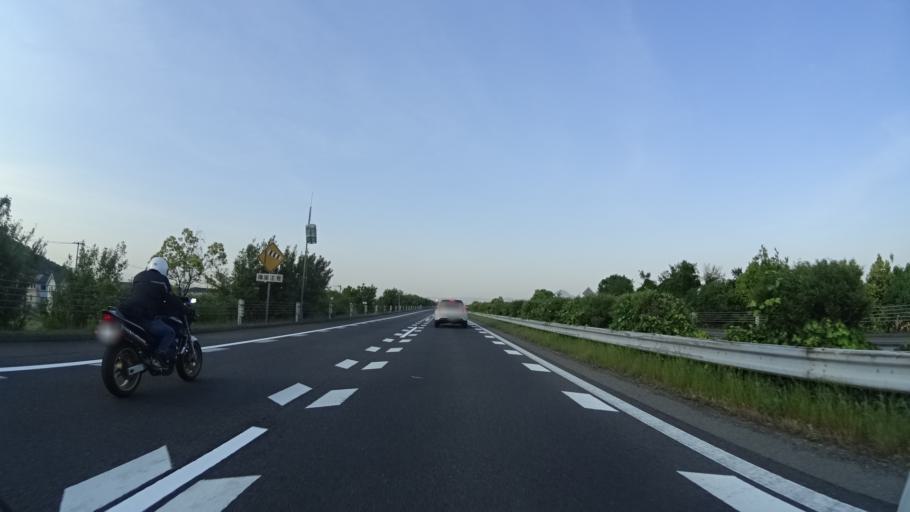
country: JP
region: Kagawa
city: Tadotsu
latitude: 34.2325
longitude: 133.7482
